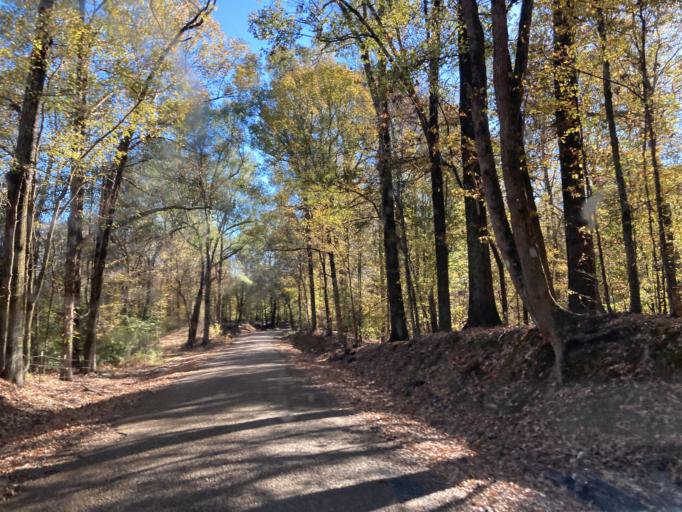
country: US
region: Mississippi
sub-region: Yazoo County
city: Yazoo City
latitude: 32.7800
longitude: -90.4072
